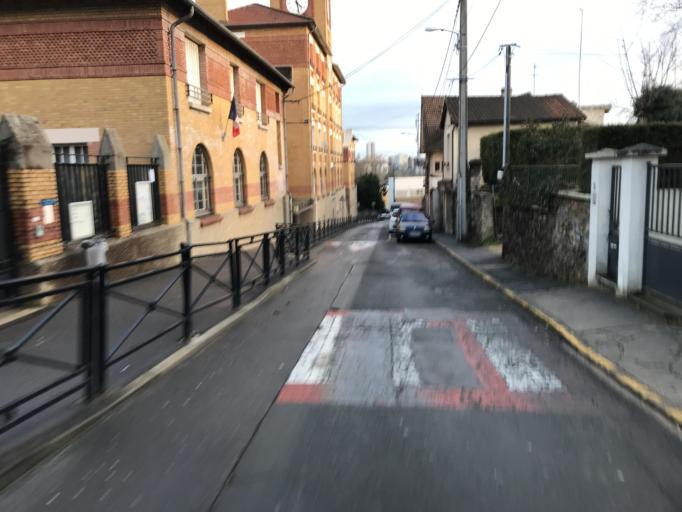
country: FR
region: Ile-de-France
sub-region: Departement de l'Essonne
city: Savigny-sur-Orge
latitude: 48.6780
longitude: 2.3492
